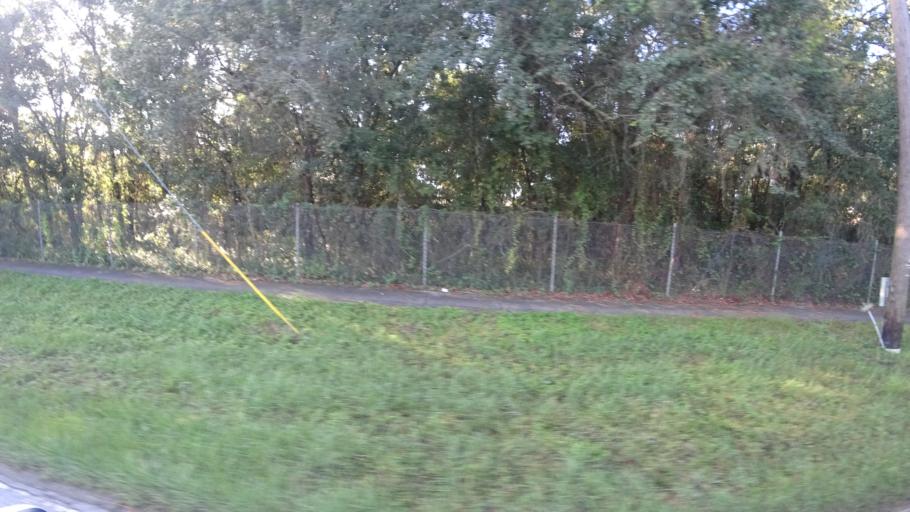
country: US
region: Florida
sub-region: Manatee County
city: Samoset
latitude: 27.4509
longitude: -82.5267
